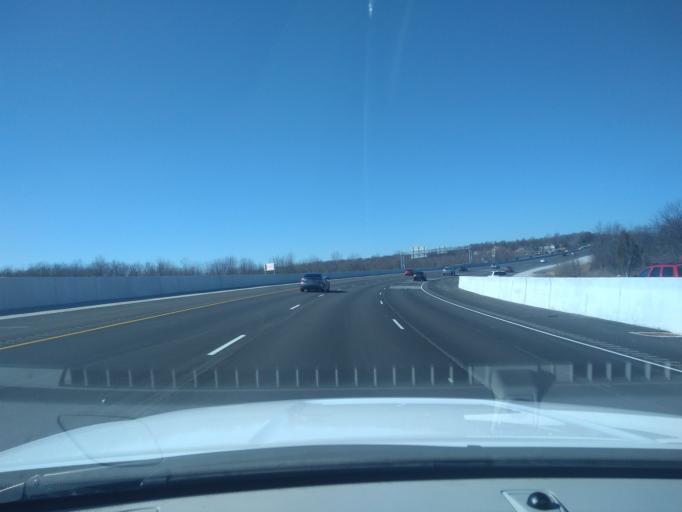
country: US
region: Arkansas
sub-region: Washington County
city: Johnson
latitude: 36.1136
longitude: -94.1737
